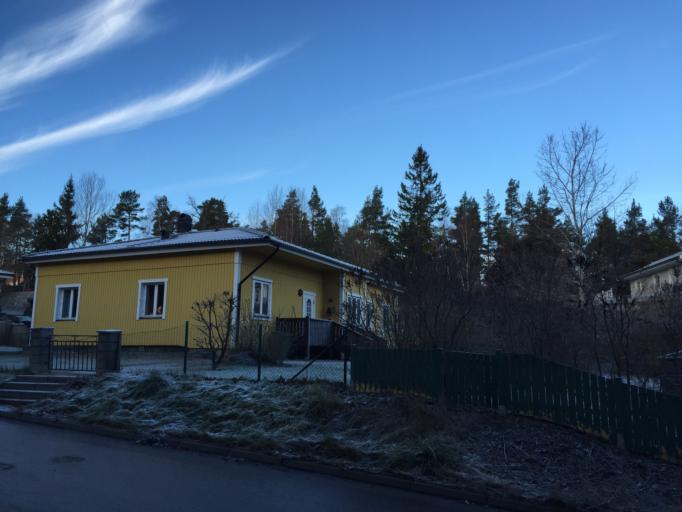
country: SE
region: Stockholm
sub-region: Salems Kommun
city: Ronninge
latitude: 59.1865
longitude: 17.7459
